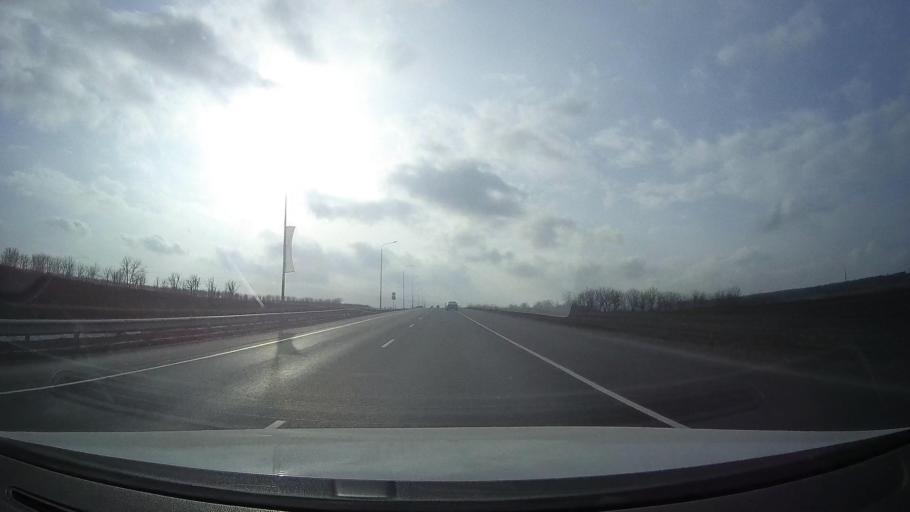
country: RU
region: Rostov
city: Grushevskaya
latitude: 47.4301
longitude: 39.8674
